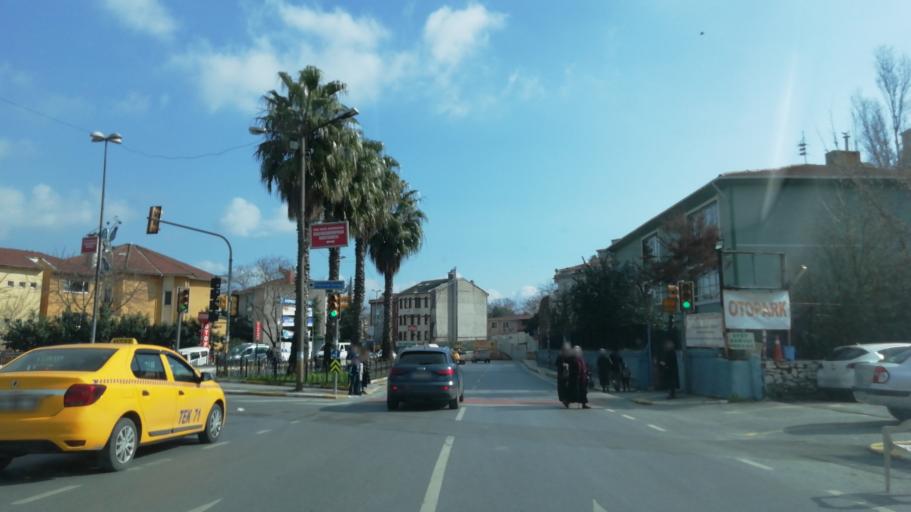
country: TR
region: Istanbul
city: Istanbul
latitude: 41.0460
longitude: 28.9327
